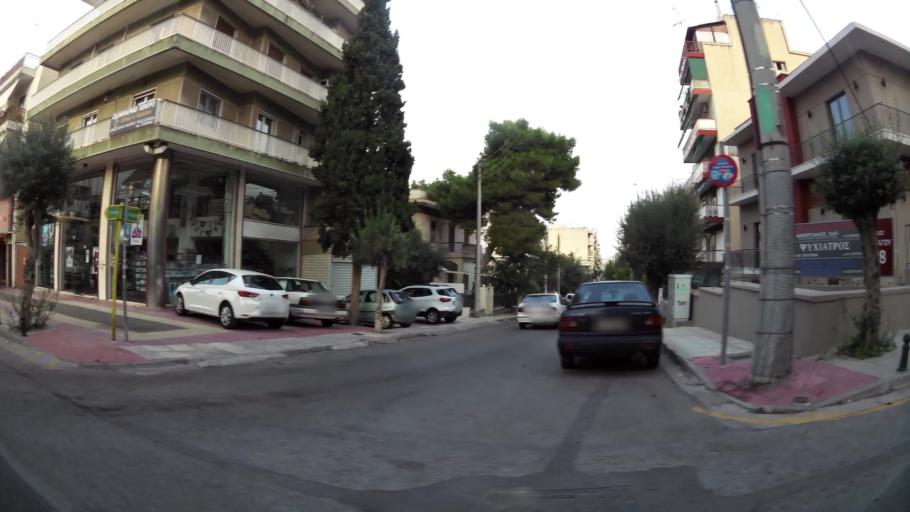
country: GR
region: Attica
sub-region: Nomarchia Athinas
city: Agios Dimitrios
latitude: 37.9397
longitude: 23.7356
